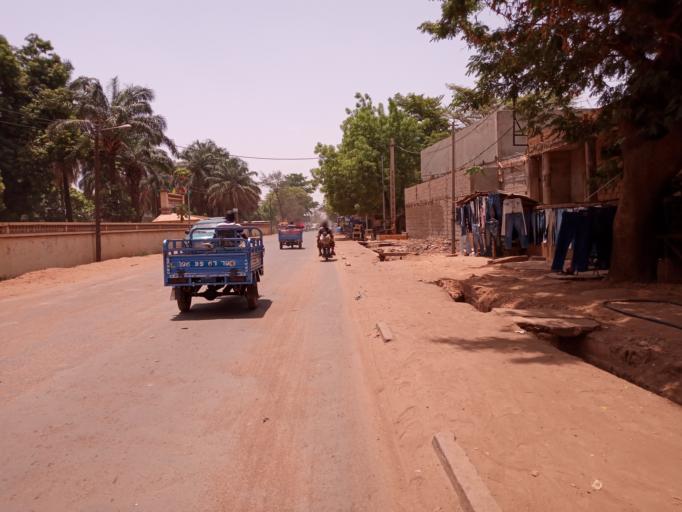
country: ML
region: Bamako
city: Bamako
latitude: 12.6486
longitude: -7.9755
